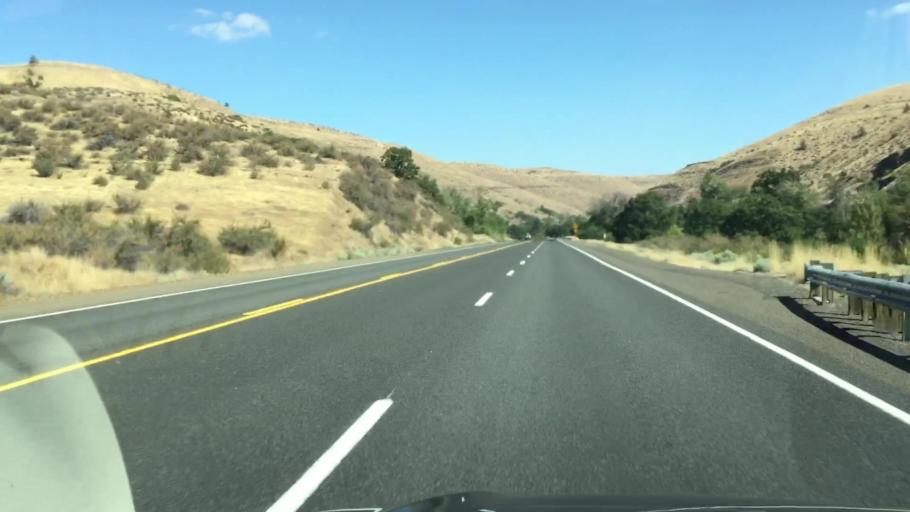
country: US
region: Oregon
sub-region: Wasco County
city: The Dalles
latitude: 45.2662
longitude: -121.1903
